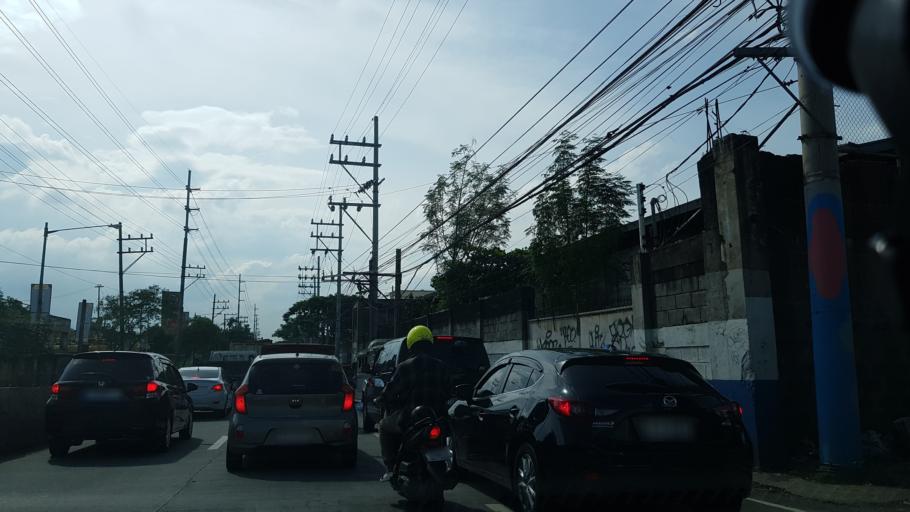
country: PH
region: Calabarzon
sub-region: Province of Rizal
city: Cainta
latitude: 14.5879
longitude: 121.1080
